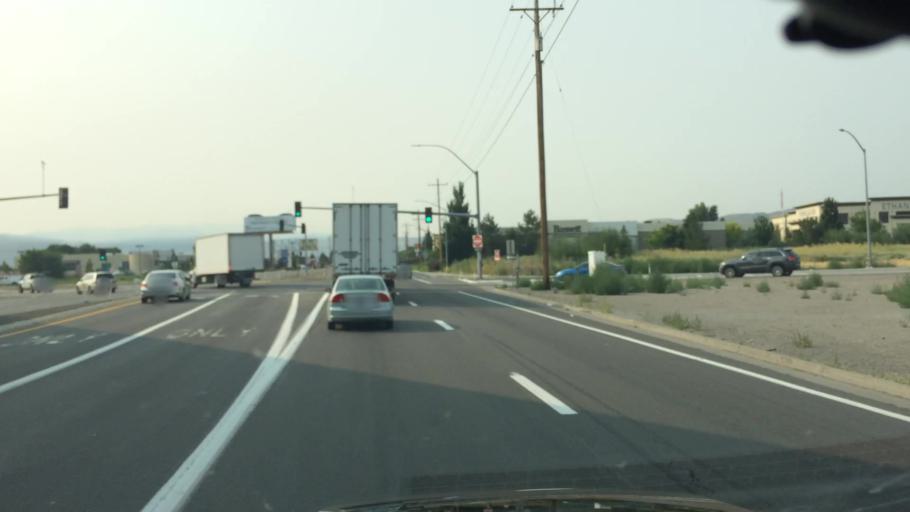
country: US
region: Nevada
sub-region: Washoe County
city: Sparks
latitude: 39.4497
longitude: -119.7760
